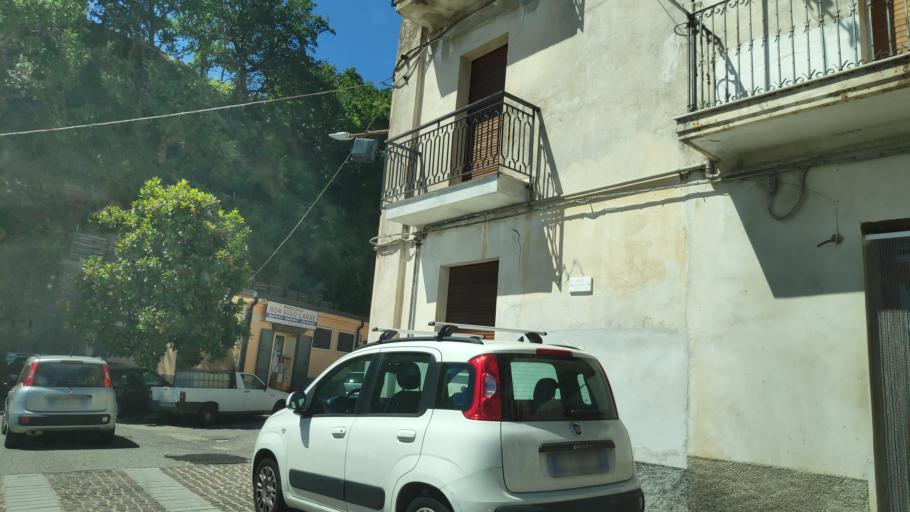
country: IT
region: Calabria
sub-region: Provincia di Catanzaro
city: Montauro
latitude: 38.7477
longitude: 16.5111
